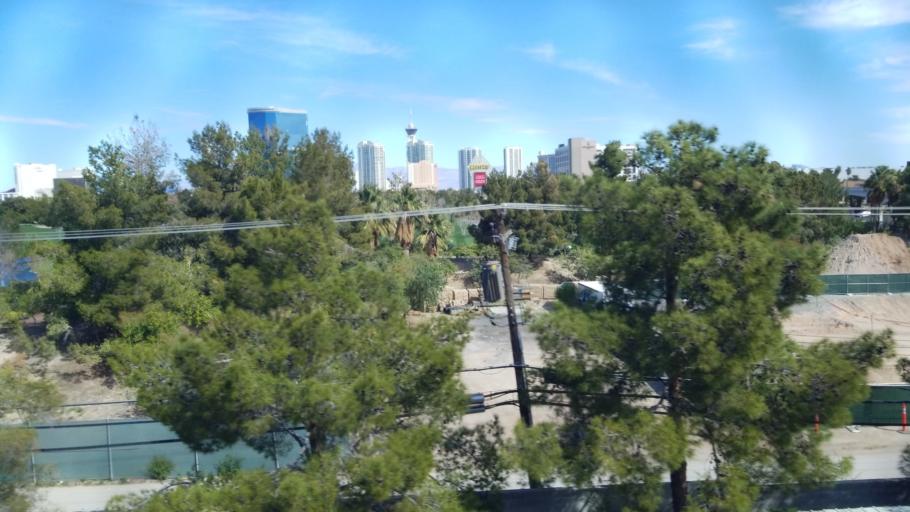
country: US
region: Nevada
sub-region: Clark County
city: Paradise
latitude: 36.1222
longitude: -115.1561
